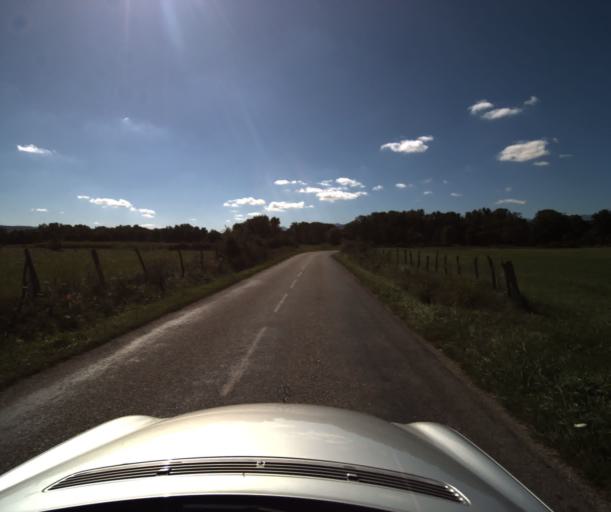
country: FR
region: Midi-Pyrenees
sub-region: Departement de l'Ariege
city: Lavelanet
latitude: 42.9913
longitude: 1.8916
